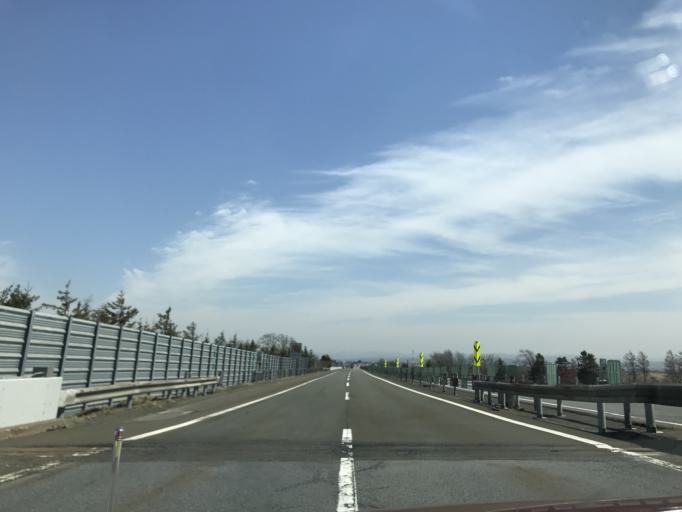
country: JP
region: Hokkaido
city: Ebetsu
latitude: 43.1343
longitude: 141.6573
